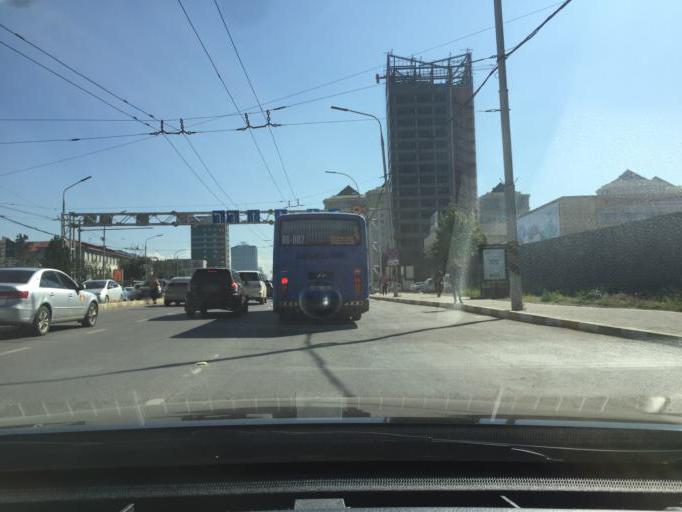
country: MN
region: Ulaanbaatar
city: Ulaanbaatar
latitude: 47.9148
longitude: 106.8913
